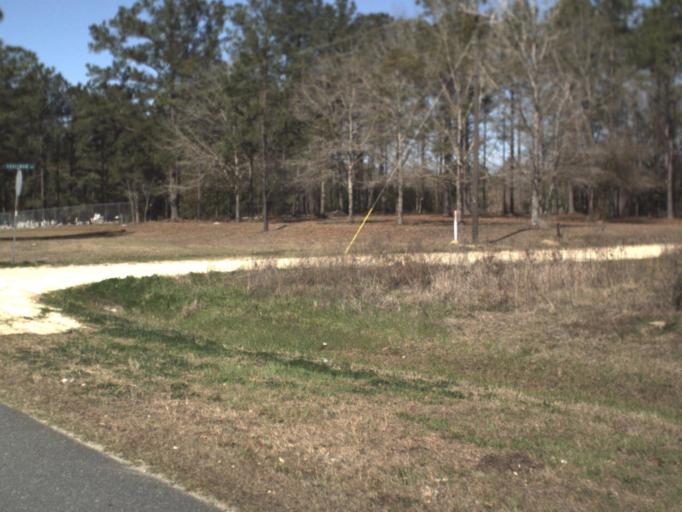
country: US
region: Florida
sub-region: Jackson County
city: Sneads
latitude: 30.7197
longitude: -85.0619
